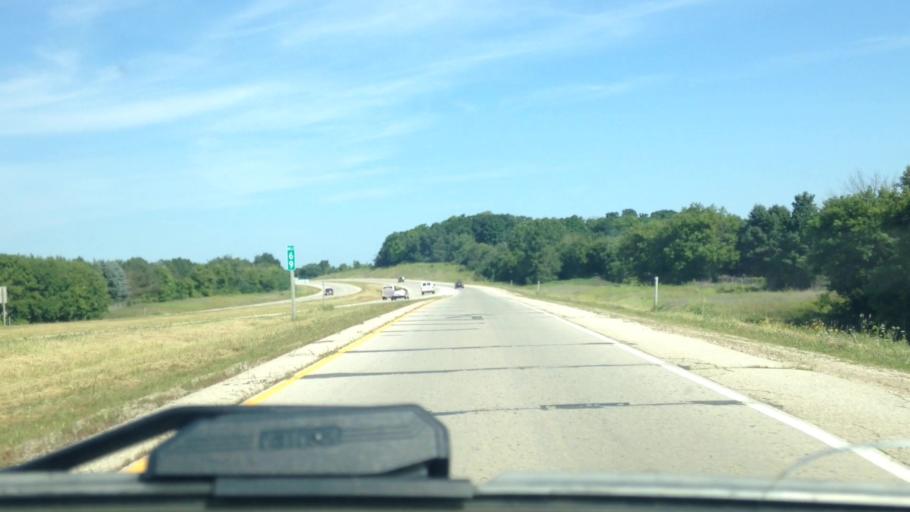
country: US
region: Wisconsin
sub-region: Washington County
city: West Bend
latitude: 43.4008
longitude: -88.1920
